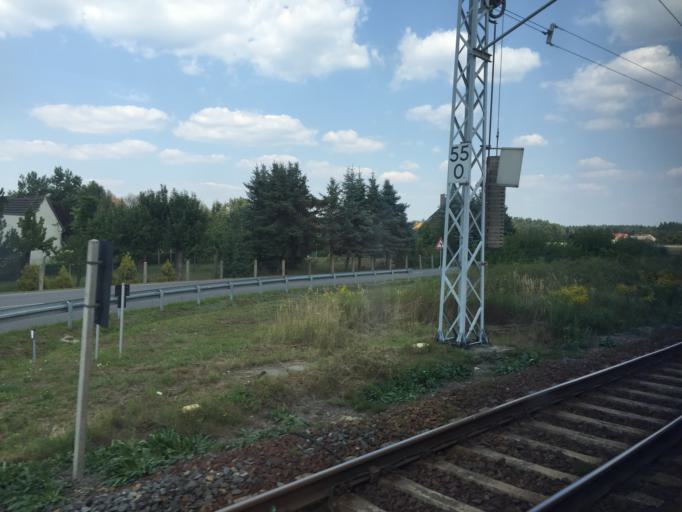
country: DE
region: Brandenburg
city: Welzow
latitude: 51.5818
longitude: 14.1124
